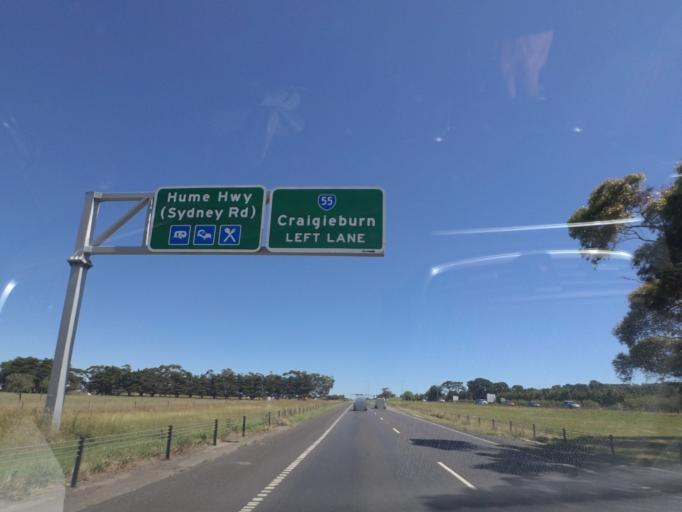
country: AU
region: Victoria
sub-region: Hume
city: Craigieburn
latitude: -37.5610
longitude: 144.9420
